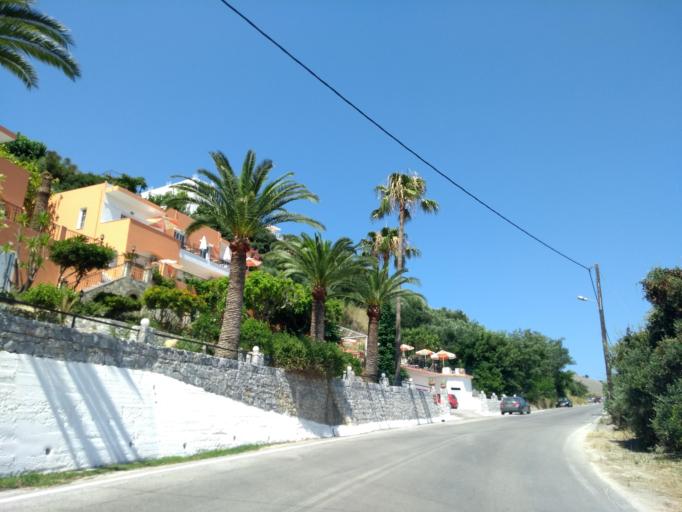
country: GR
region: Crete
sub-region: Nomos Chanias
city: Georgioupolis
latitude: 35.3732
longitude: 24.2446
